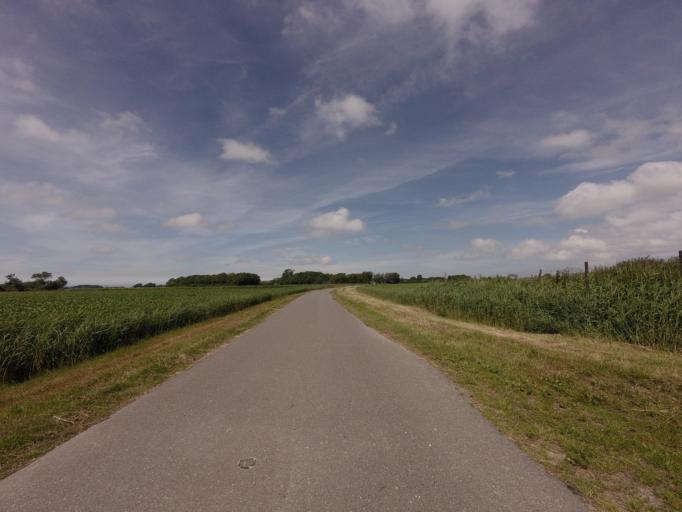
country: NL
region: North Holland
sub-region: Gemeente Texel
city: Den Burg
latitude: 53.0801
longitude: 4.8817
